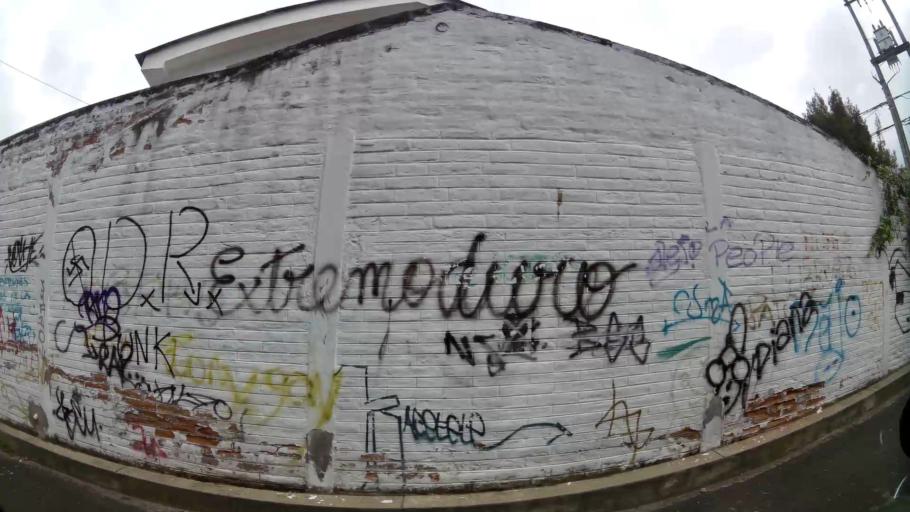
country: EC
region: Pichincha
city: Quito
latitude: -0.1298
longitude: -78.4958
